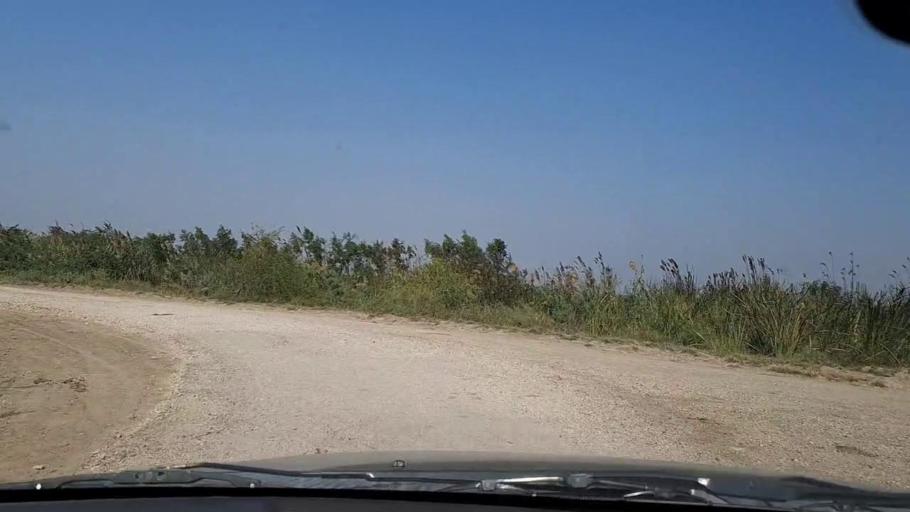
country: PK
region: Sindh
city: Chuhar Jamali
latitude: 24.4402
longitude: 67.7998
